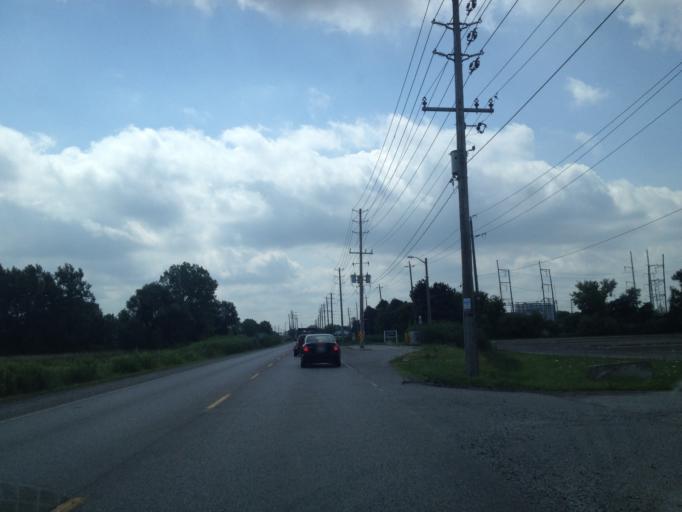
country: CA
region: Ontario
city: London
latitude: 43.0328
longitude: -81.1903
